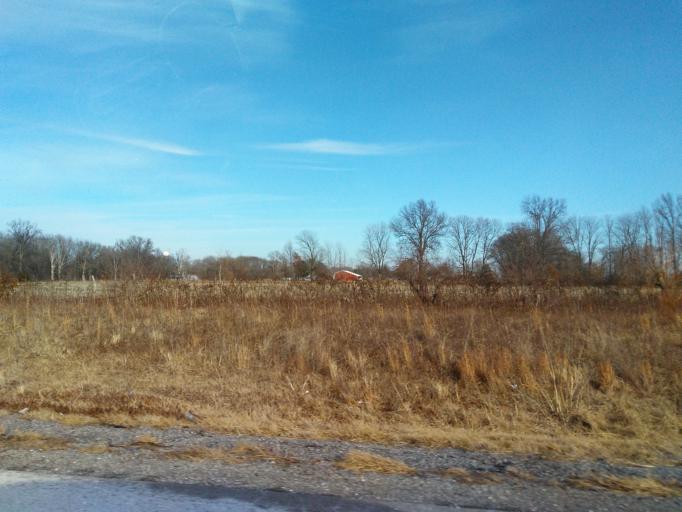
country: US
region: Illinois
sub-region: Jefferson County
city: Ina
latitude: 38.1476
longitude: -88.9128
